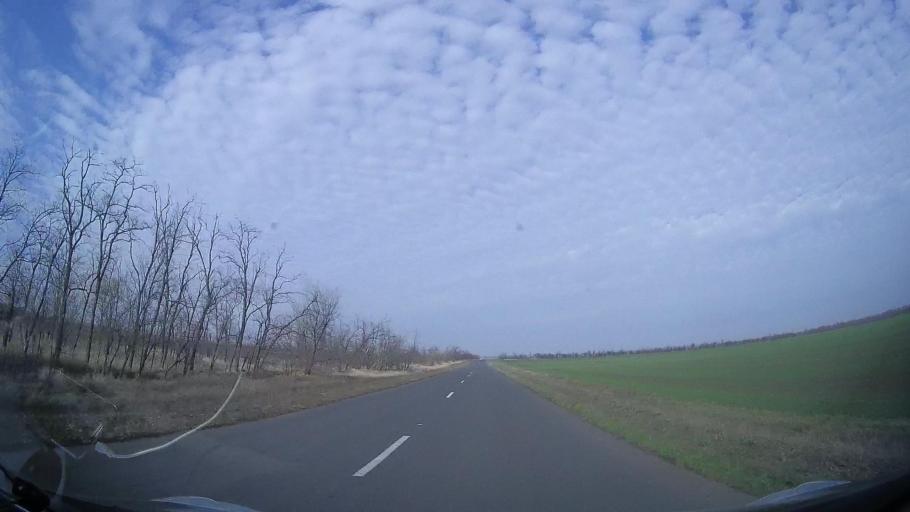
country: RU
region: Rostov
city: Gigant
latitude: 46.8553
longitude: 41.2824
